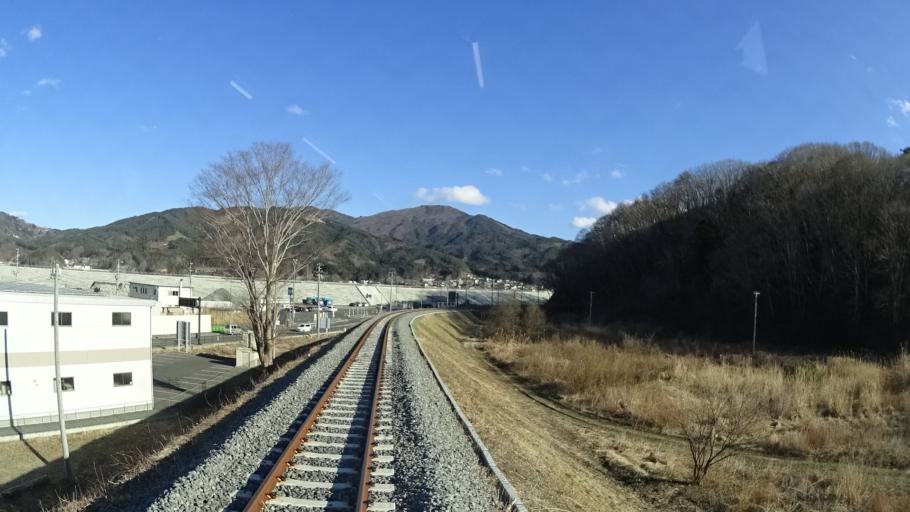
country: JP
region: Iwate
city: Miyako
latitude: 39.5913
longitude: 141.9447
